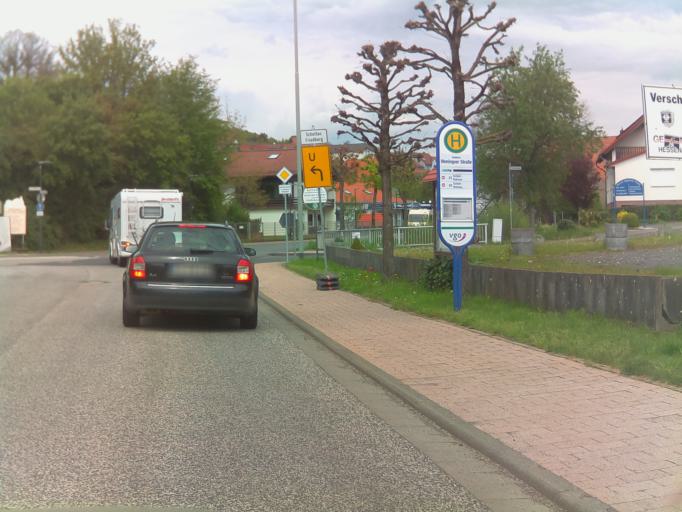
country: DE
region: Hesse
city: Gedern
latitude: 50.4188
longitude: 9.1971
